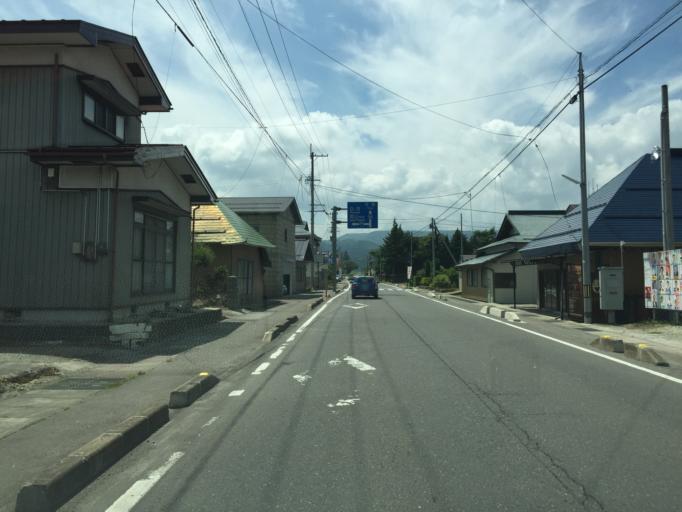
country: JP
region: Fukushima
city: Inawashiro
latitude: 37.3916
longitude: 140.0886
